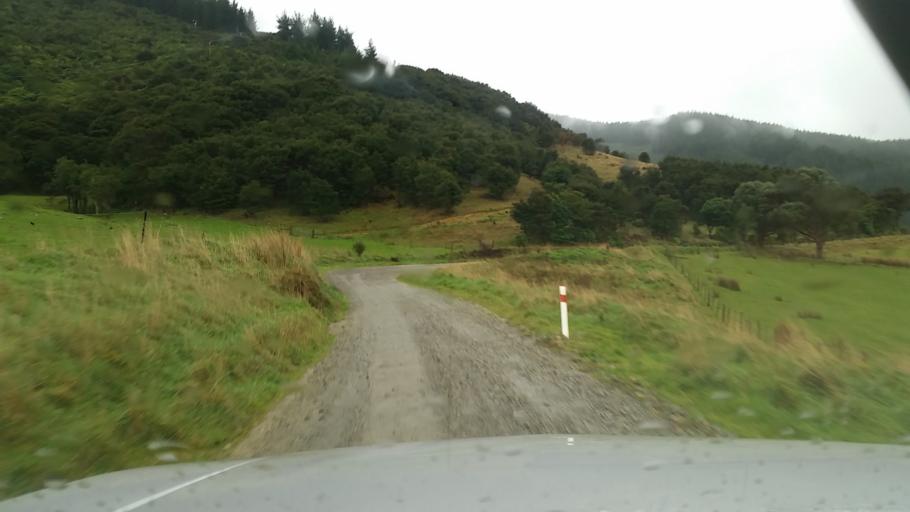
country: NZ
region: Marlborough
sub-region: Marlborough District
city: Picton
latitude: -41.1472
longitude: 174.0503
